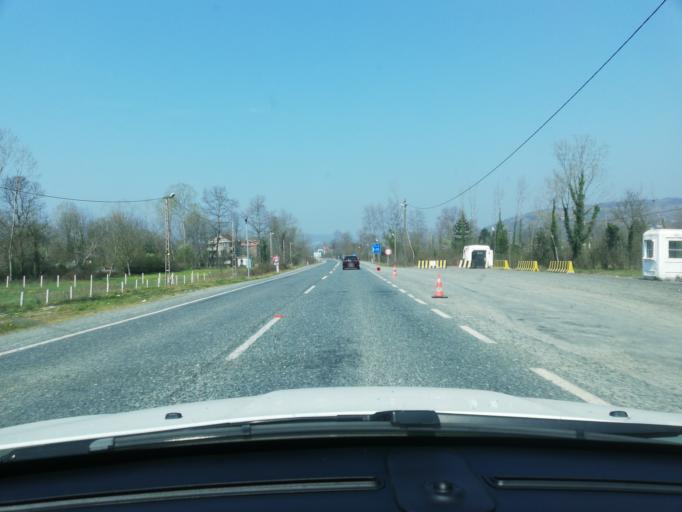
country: TR
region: Zonguldak
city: Gokcebey
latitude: 41.2985
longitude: 32.1234
